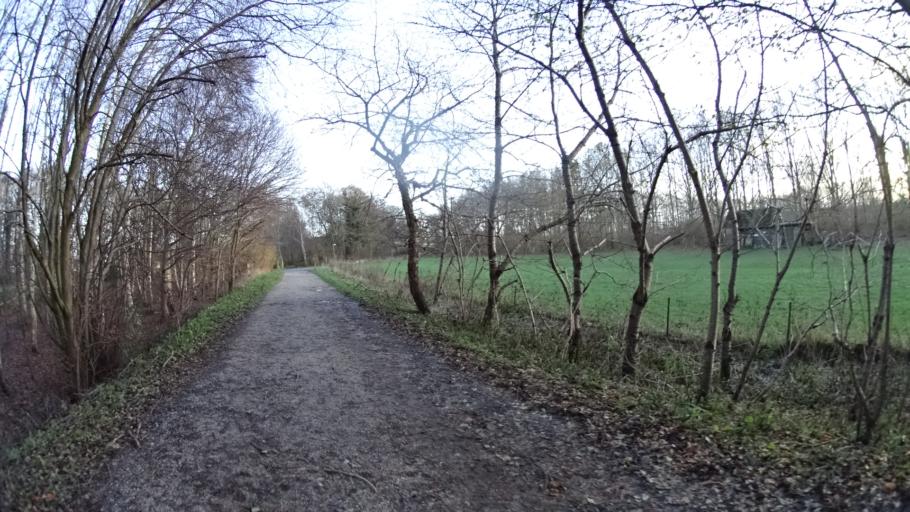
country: DK
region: Central Jutland
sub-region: Arhus Kommune
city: Stavtrup
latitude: 56.1397
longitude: 10.1174
